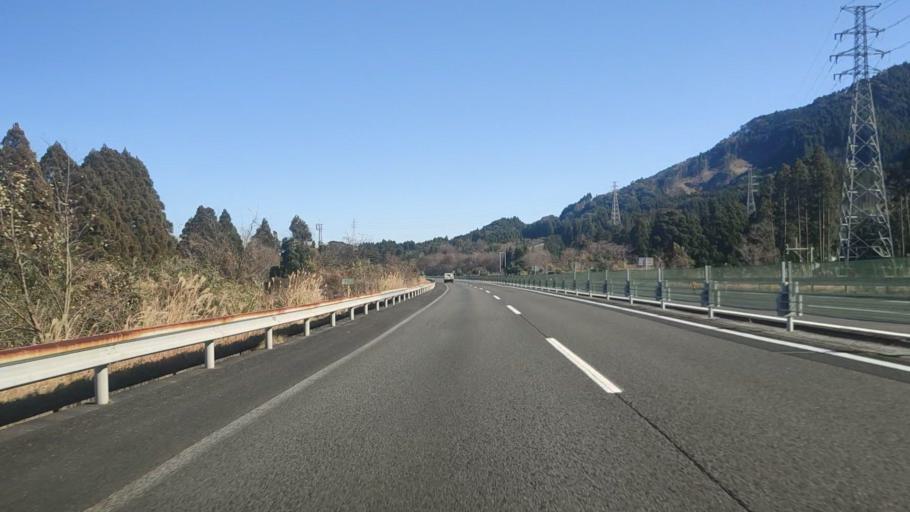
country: JP
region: Miyazaki
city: Miyazaki-shi
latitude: 31.8330
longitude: 131.3346
